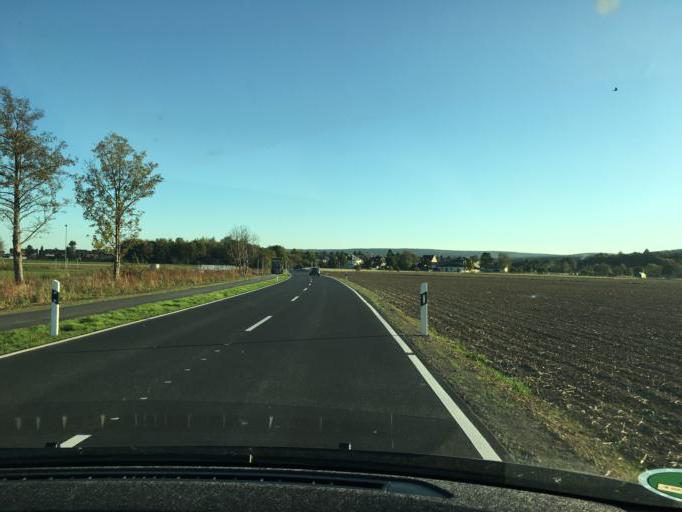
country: DE
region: North Rhine-Westphalia
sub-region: Regierungsbezirk Koln
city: Langerwehe
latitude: 50.8067
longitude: 6.3956
